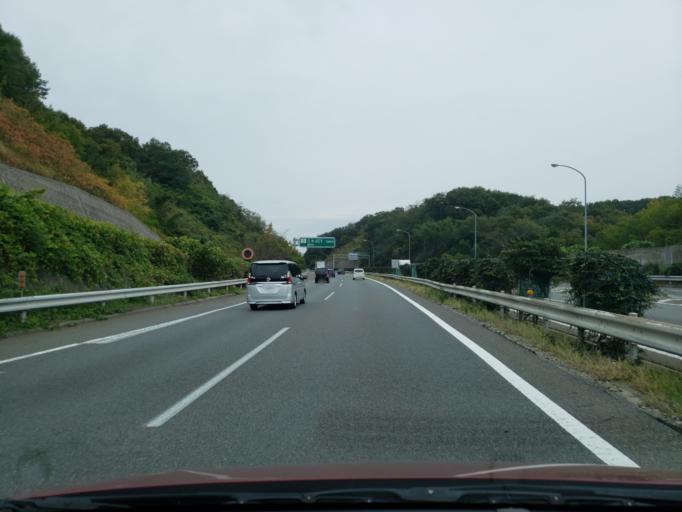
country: JP
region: Hyogo
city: Miki
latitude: 34.7981
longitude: 135.0566
